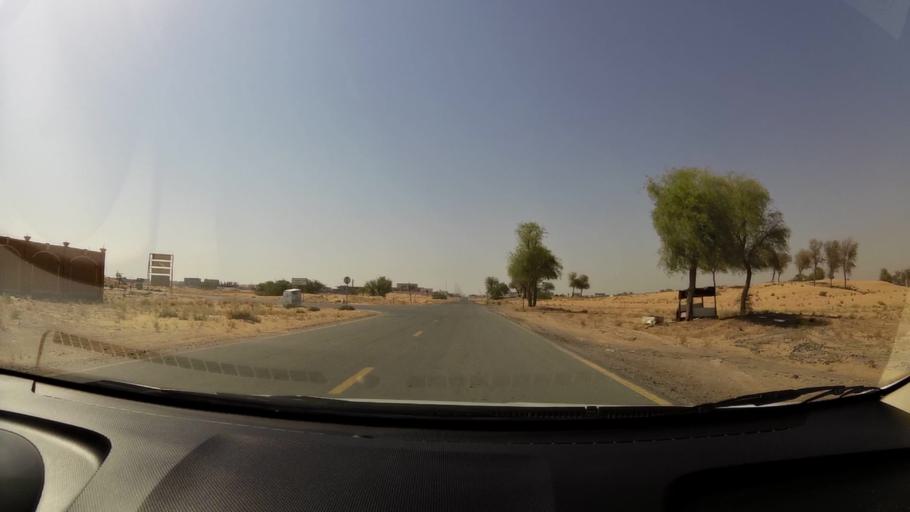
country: AE
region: Umm al Qaywayn
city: Umm al Qaywayn
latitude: 25.4777
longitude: 55.6166
